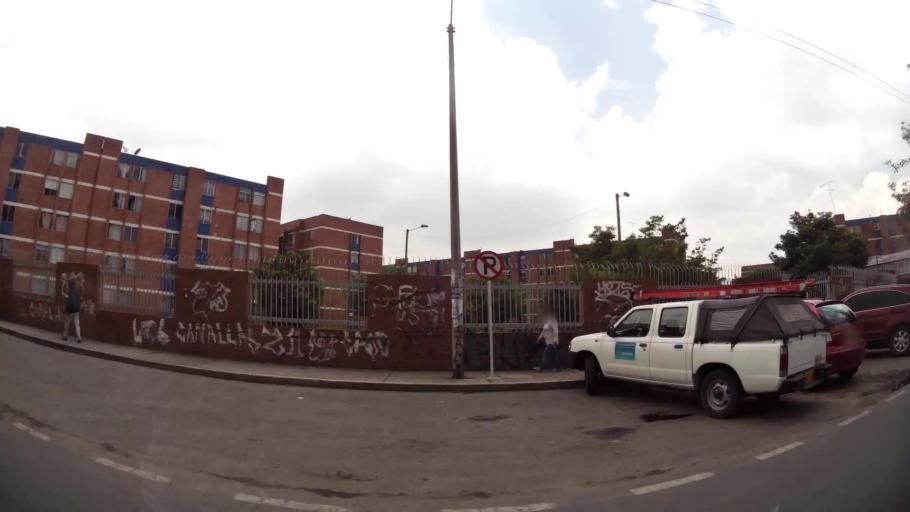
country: CO
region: Cundinamarca
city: Cota
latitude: 4.7490
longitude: -74.0524
